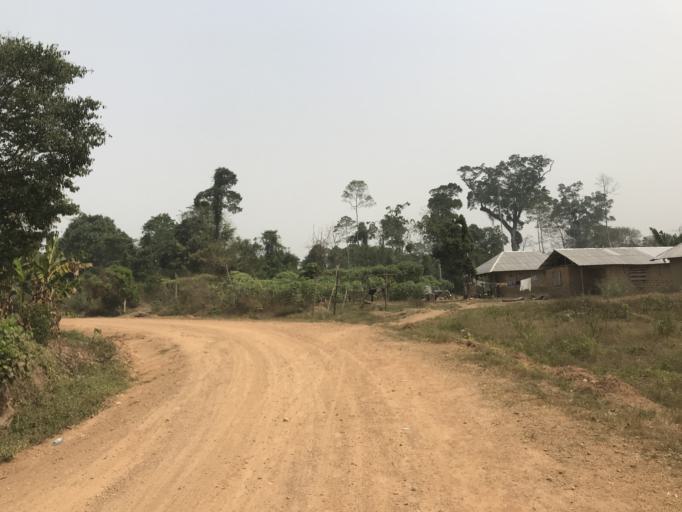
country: NG
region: Osun
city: Ifetedo
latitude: 7.0254
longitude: 4.4455
